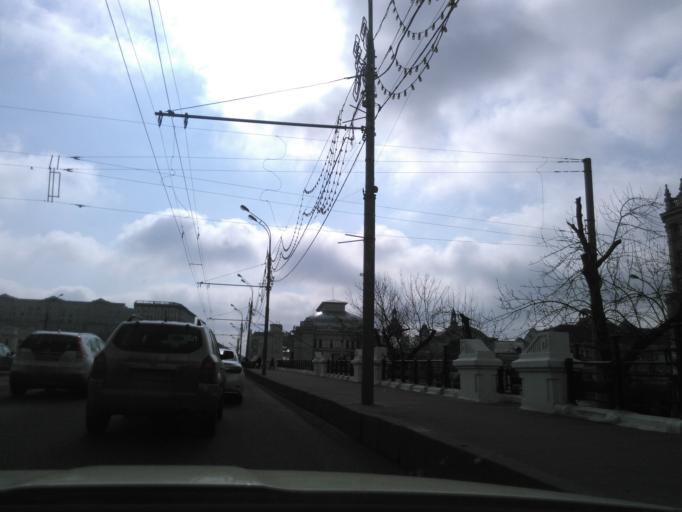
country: RU
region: Moskovskaya
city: Dorogomilovo
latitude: 55.7783
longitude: 37.5808
